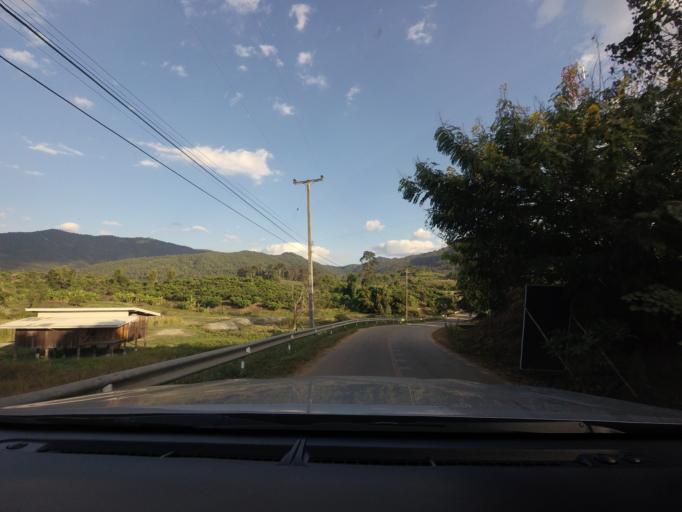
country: TH
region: Chiang Mai
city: Phrao
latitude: 19.5136
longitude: 99.1725
